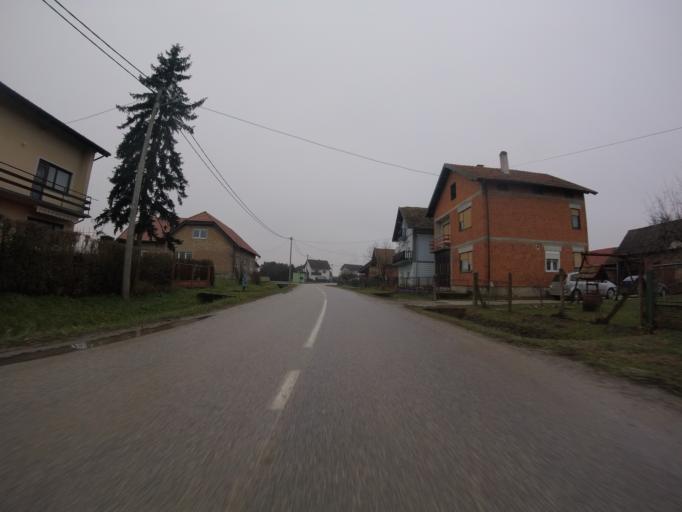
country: HR
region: Sisacko-Moslavacka
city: Lekenik
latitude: 45.6580
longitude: 16.2547
